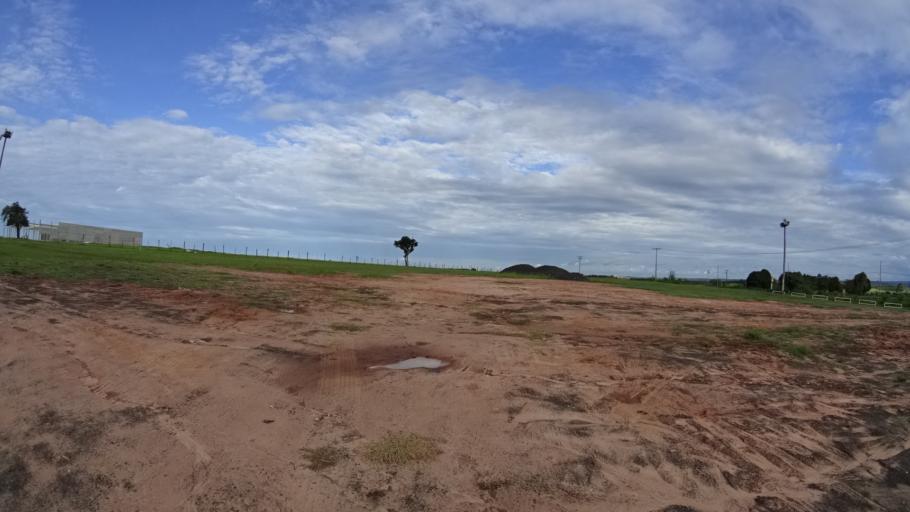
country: BR
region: Sao Paulo
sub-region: Marilia
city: Marilia
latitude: -22.2218
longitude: -49.8807
